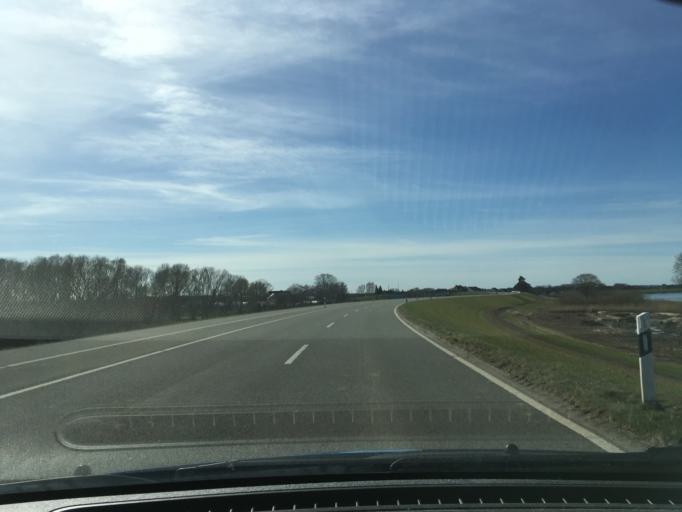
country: DE
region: Lower Saxony
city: Winsen
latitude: 53.3942
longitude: 10.1858
